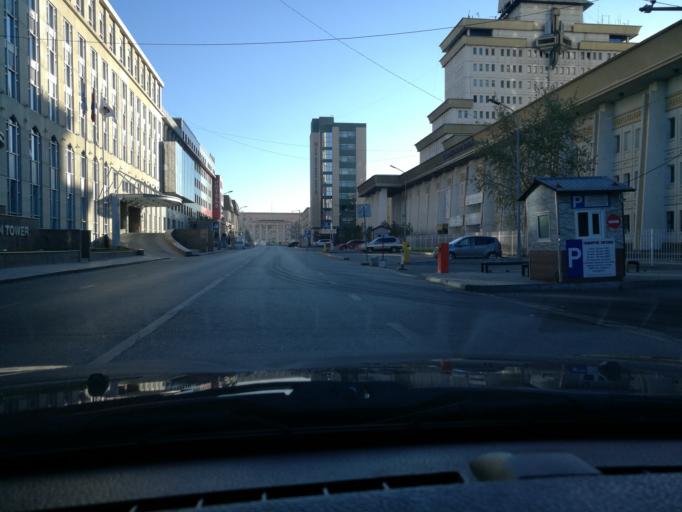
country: MN
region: Ulaanbaatar
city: Ulaanbaatar
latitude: 47.9201
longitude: 106.9200
